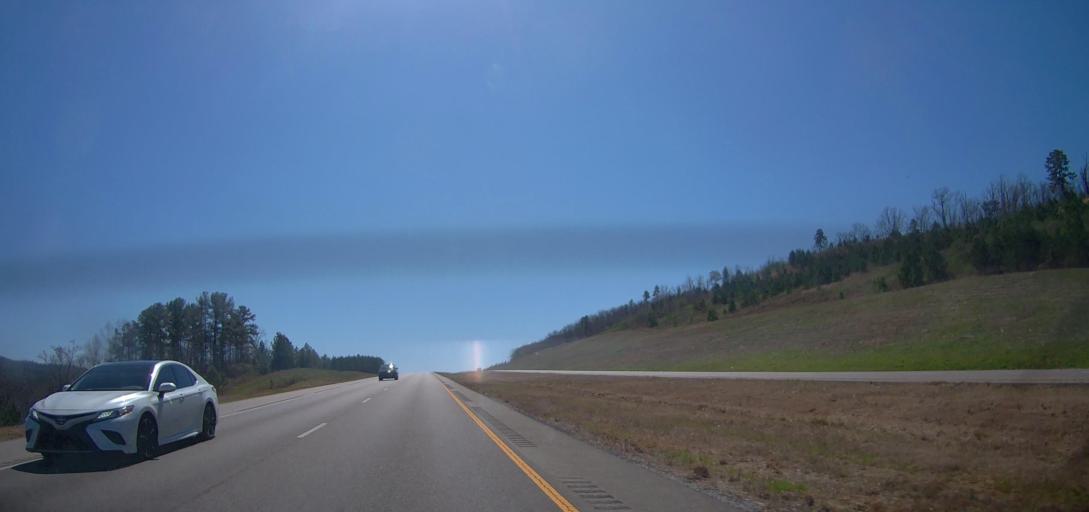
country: US
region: Alabama
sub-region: Calhoun County
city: Saks
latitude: 33.6903
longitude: -85.8052
